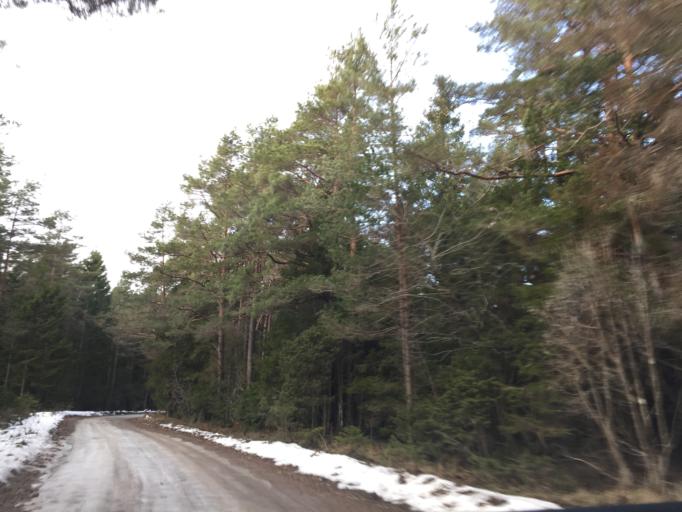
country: EE
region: Saare
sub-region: Kuressaare linn
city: Kuressaare
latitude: 58.4864
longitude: 21.9416
